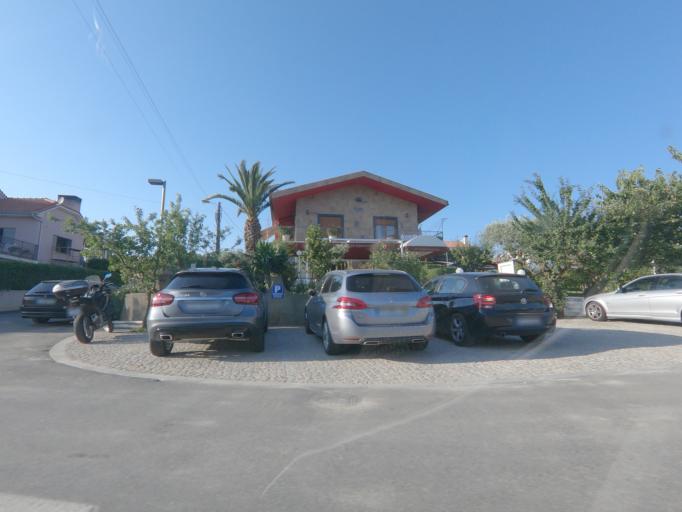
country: PT
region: Vila Real
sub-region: Sabrosa
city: Vilela
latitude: 41.2673
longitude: -7.6278
